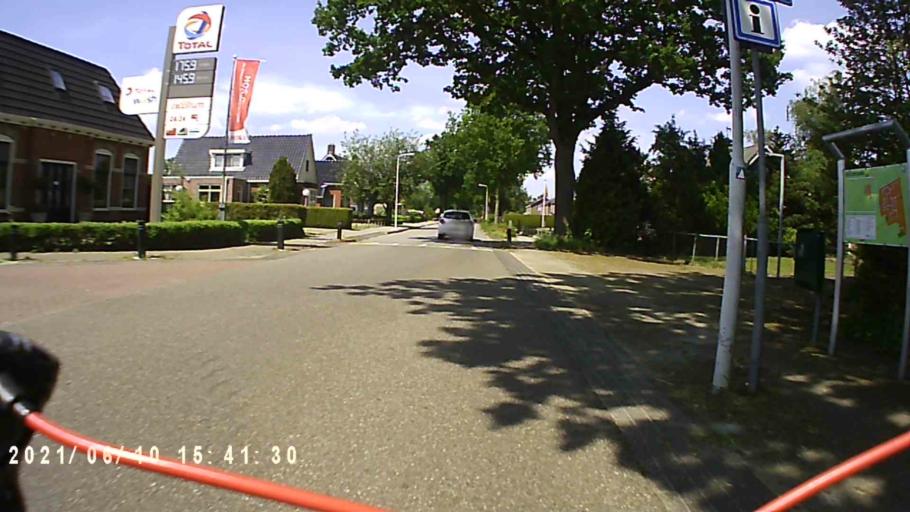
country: NL
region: Friesland
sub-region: Gemeente Achtkarspelen
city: Boelenslaan
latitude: 53.1636
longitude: 6.1451
